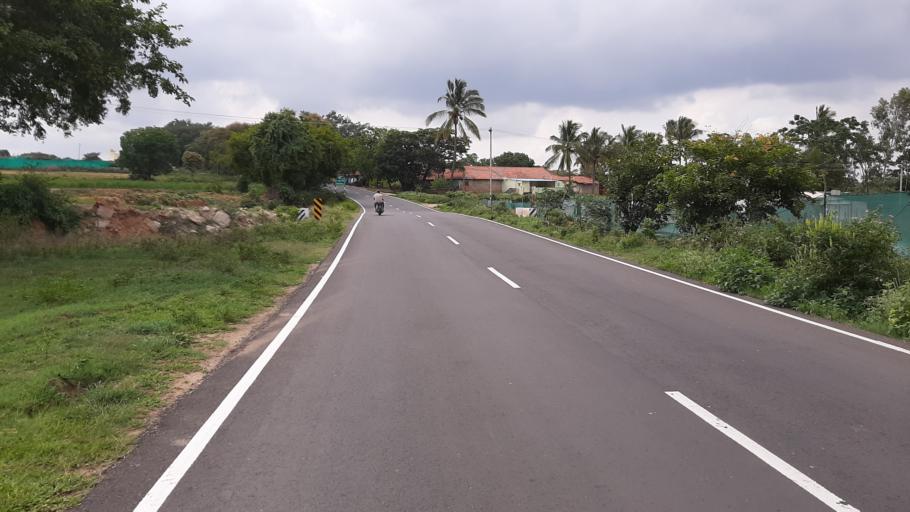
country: IN
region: Tamil Nadu
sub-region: Krishnagiri
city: Denkanikota
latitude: 12.5362
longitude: 77.7732
